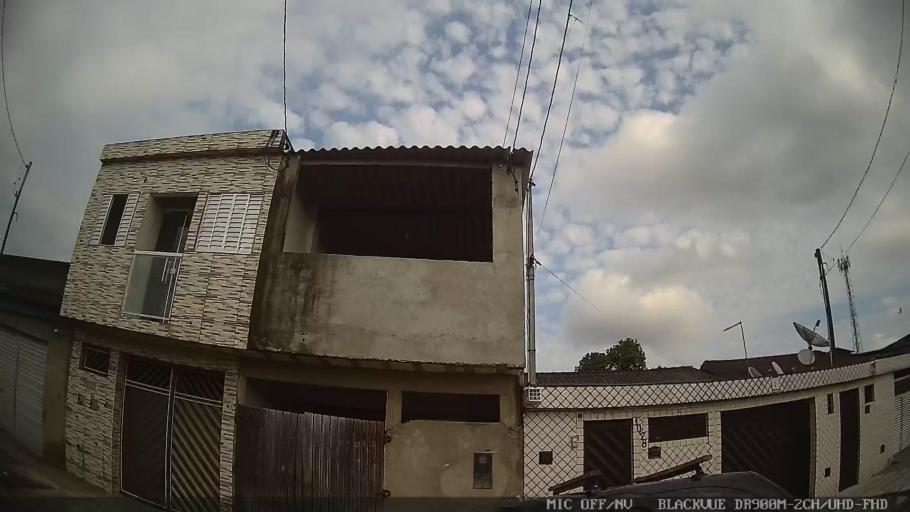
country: BR
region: Sao Paulo
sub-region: Guaruja
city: Guaruja
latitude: -23.9572
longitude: -46.2766
